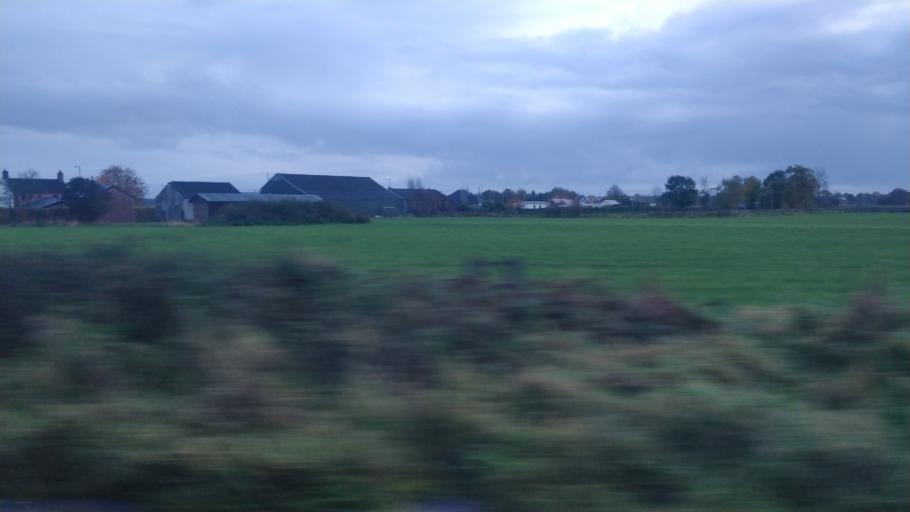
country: GB
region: England
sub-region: Lancashire
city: Parbold
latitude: 53.5985
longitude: -2.8073
